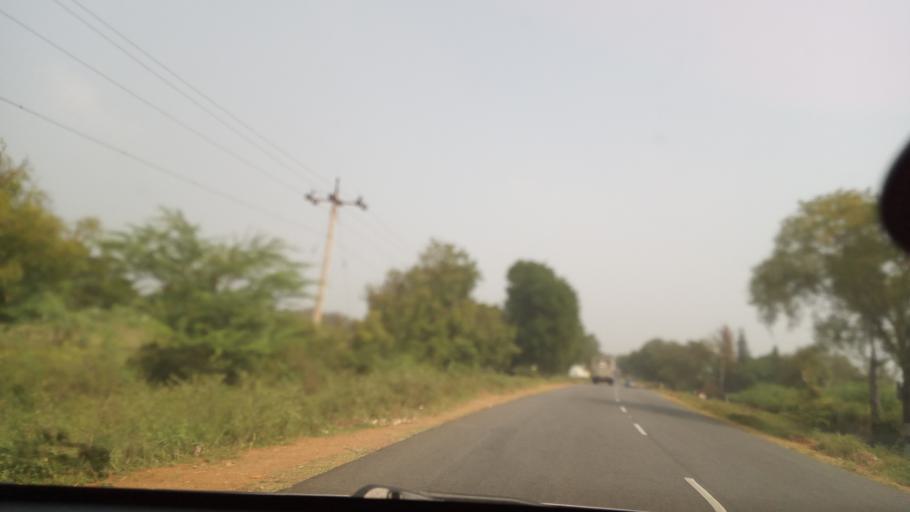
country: IN
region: Tamil Nadu
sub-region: Erode
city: Punjai Puliyampatti
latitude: 11.4116
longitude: 77.1930
